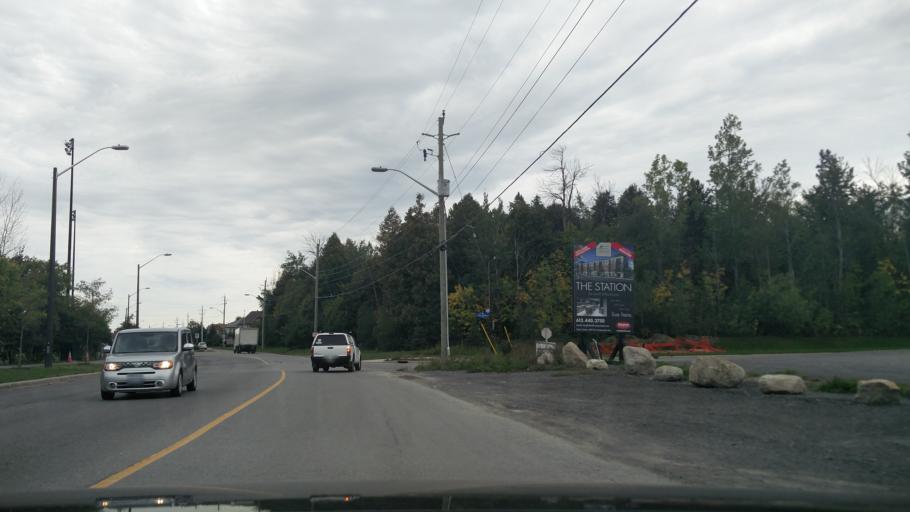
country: CA
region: Ontario
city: Bells Corners
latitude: 45.2824
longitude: -75.7448
